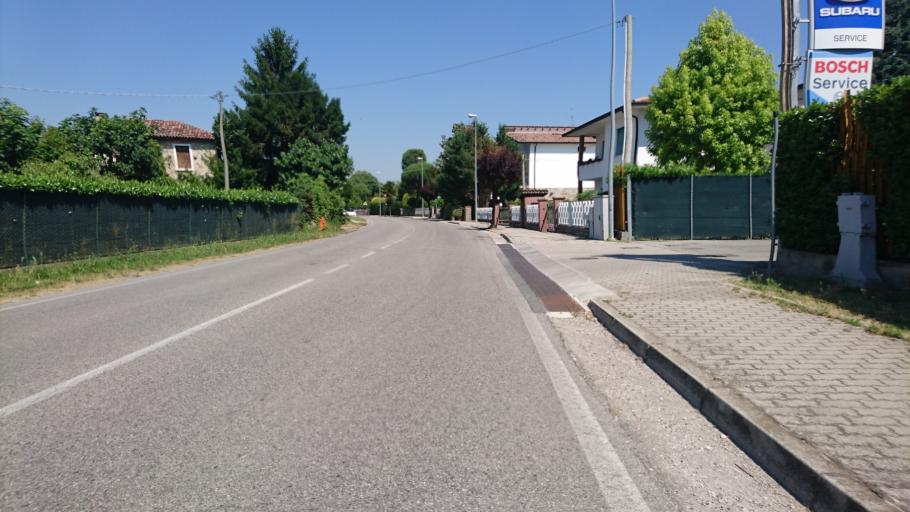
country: IT
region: Veneto
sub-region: Provincia di Padova
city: Montemerlo
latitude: 45.3882
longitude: 11.7018
